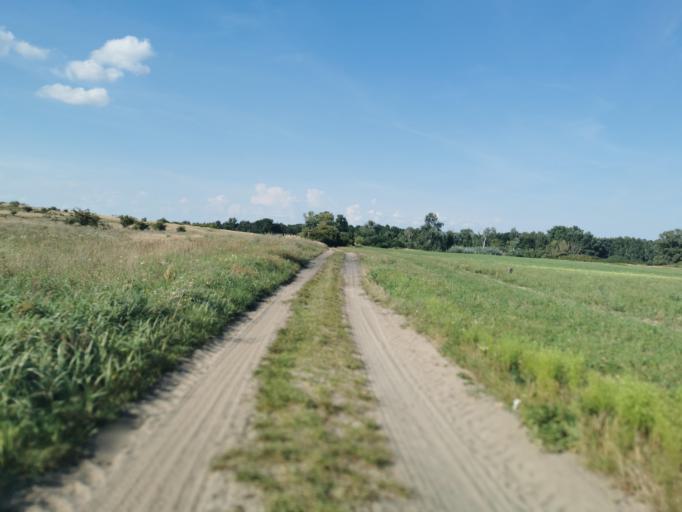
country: SK
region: Trnavsky
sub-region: Okres Senica
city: Senica
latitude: 48.6217
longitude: 17.2319
